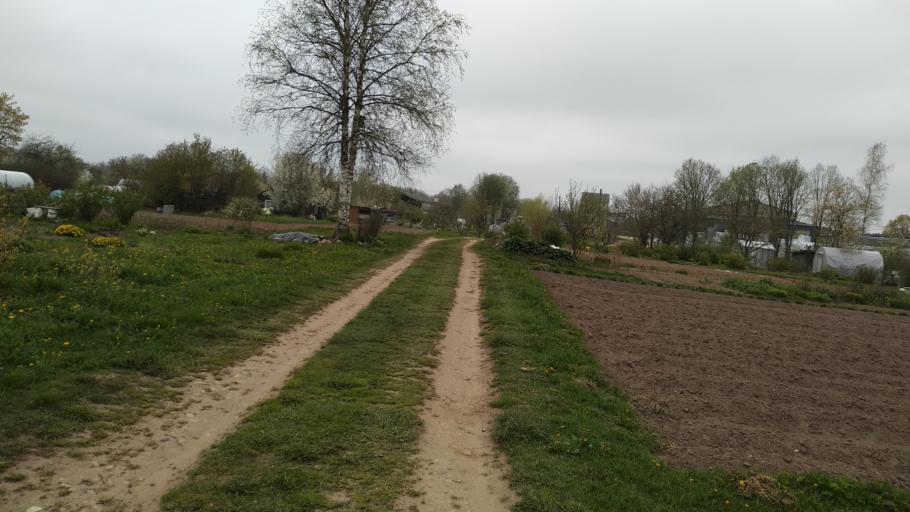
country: LV
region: Malpils
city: Malpils
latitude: 57.0137
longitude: 24.9594
